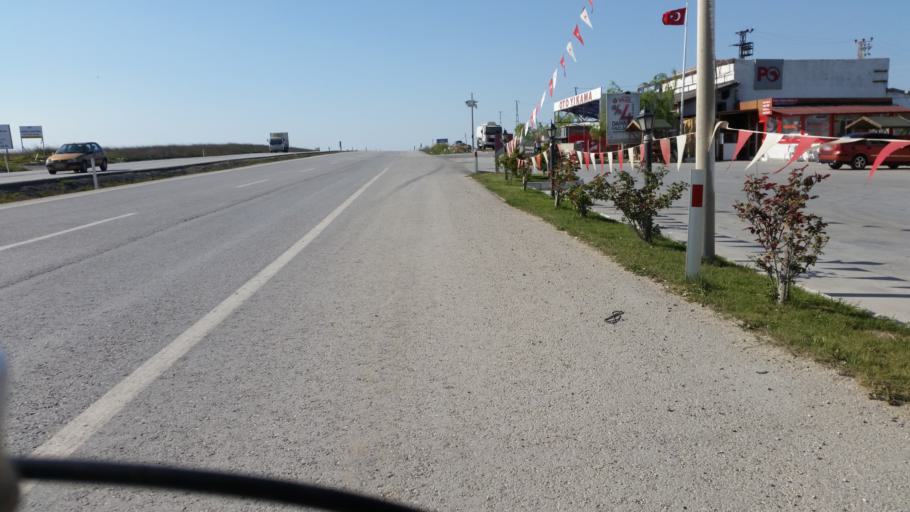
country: TR
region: Tekirdag
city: Cerkezkoey
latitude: 41.3413
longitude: 27.9653
